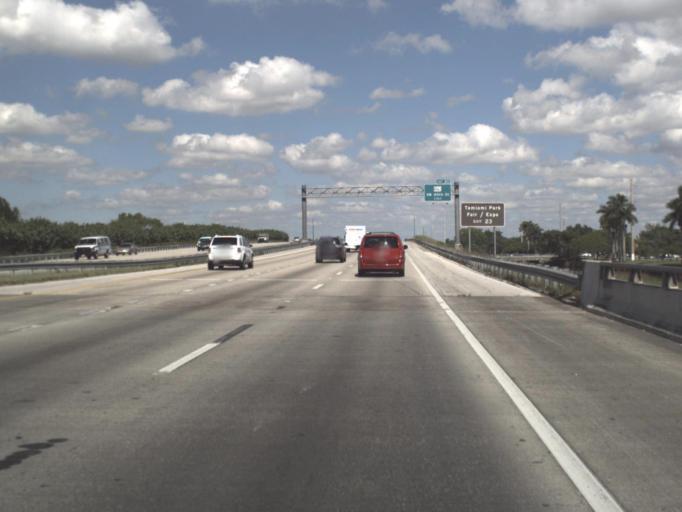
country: US
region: Florida
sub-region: Miami-Dade County
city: Westwood Lake
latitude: 25.7118
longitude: -80.3833
